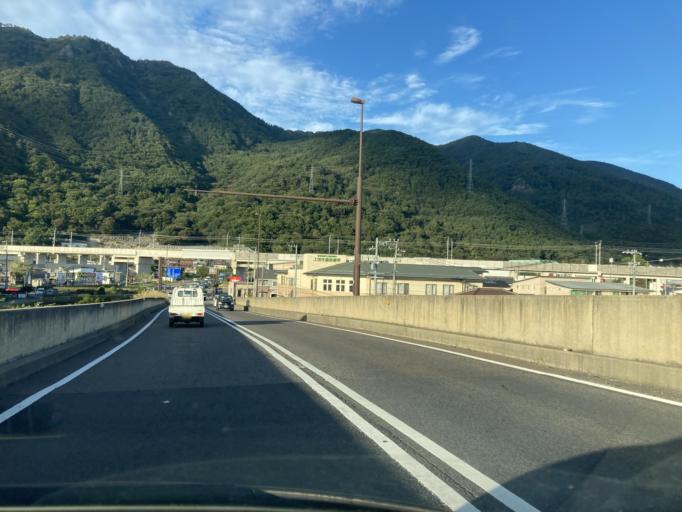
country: JP
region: Nagano
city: Ueda
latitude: 36.4142
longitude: 138.2202
